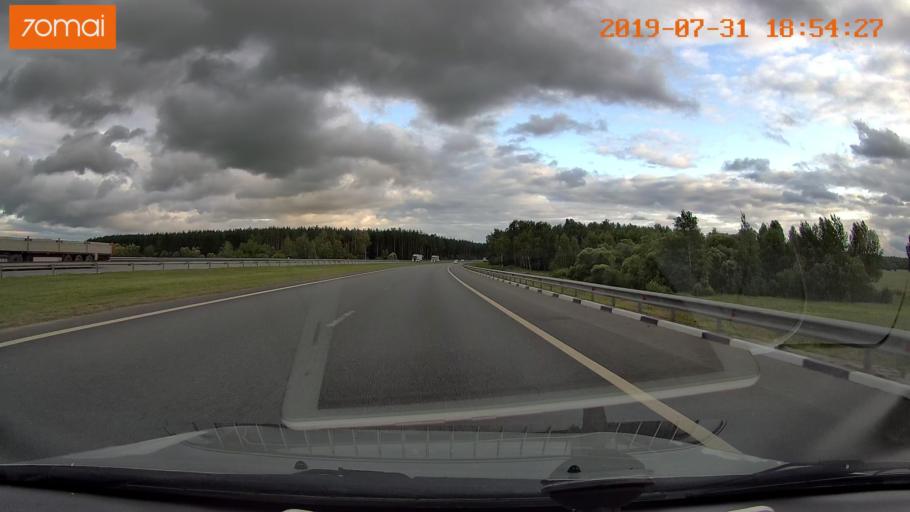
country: RU
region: Moskovskaya
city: Raduzhnyy
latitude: 55.1898
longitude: 38.6682
